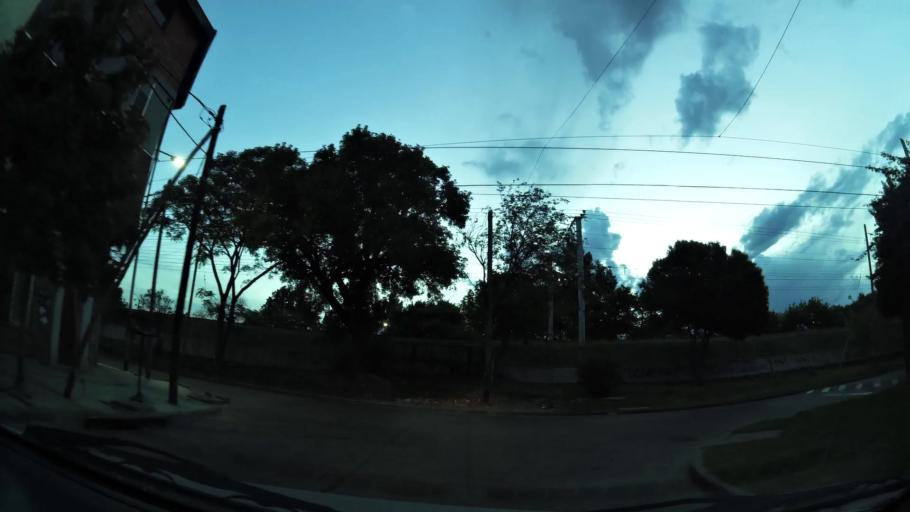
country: AR
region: Buenos Aires
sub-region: Partido de Avellaneda
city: Avellaneda
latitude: -34.6831
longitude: -58.3362
